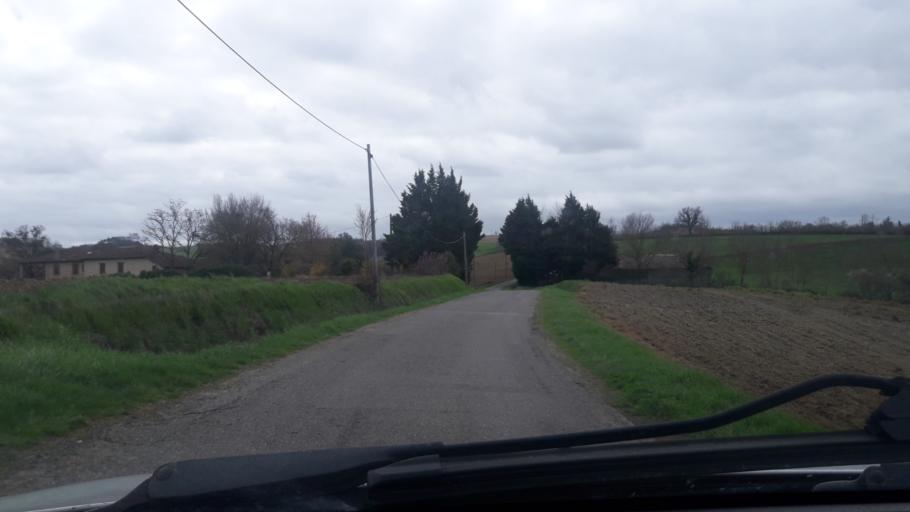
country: FR
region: Midi-Pyrenees
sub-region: Departement de l'Ariege
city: Lezat-sur-Leze
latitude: 43.2125
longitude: 1.3061
